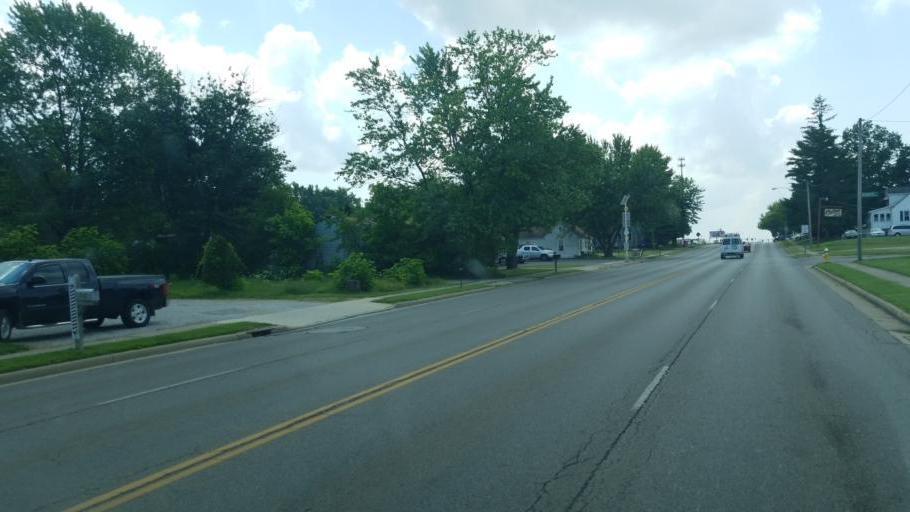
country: US
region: Ohio
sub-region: Richland County
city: Mansfield
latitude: 40.7804
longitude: -82.5520
